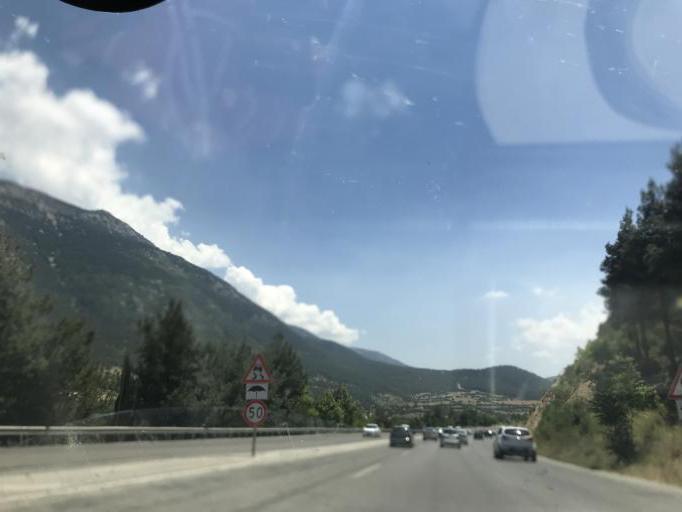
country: TR
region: Denizli
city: Honaz
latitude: 37.7233
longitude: 29.2073
